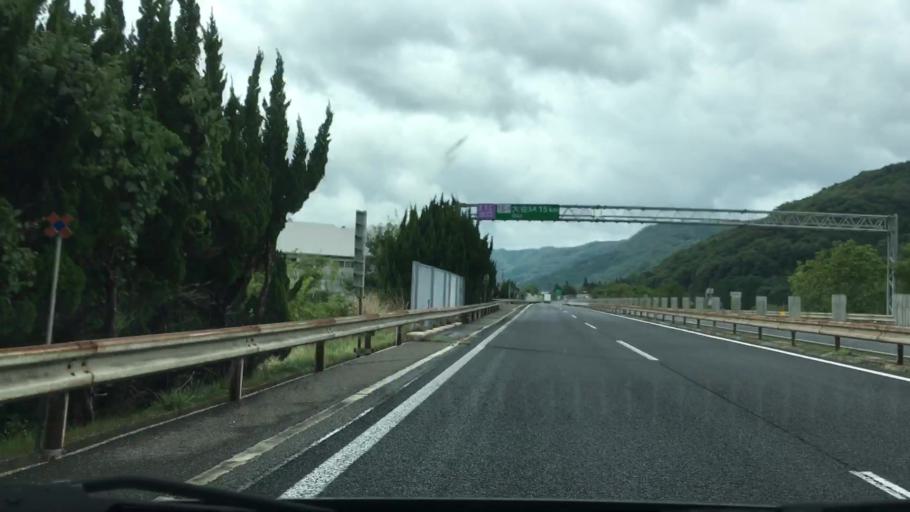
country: JP
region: Okayama
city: Niimi
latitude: 34.9717
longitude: 133.6515
